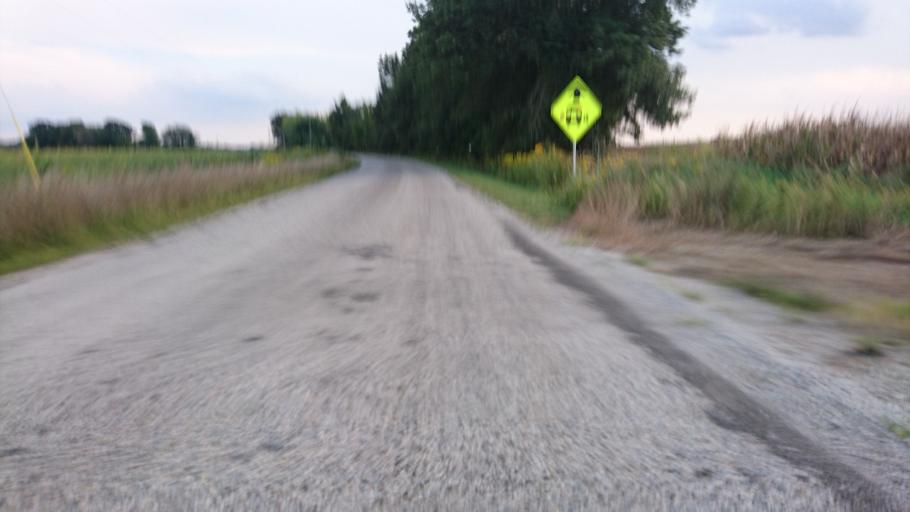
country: US
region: Illinois
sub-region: Logan County
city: Atlanta
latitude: 40.2306
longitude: -89.2048
